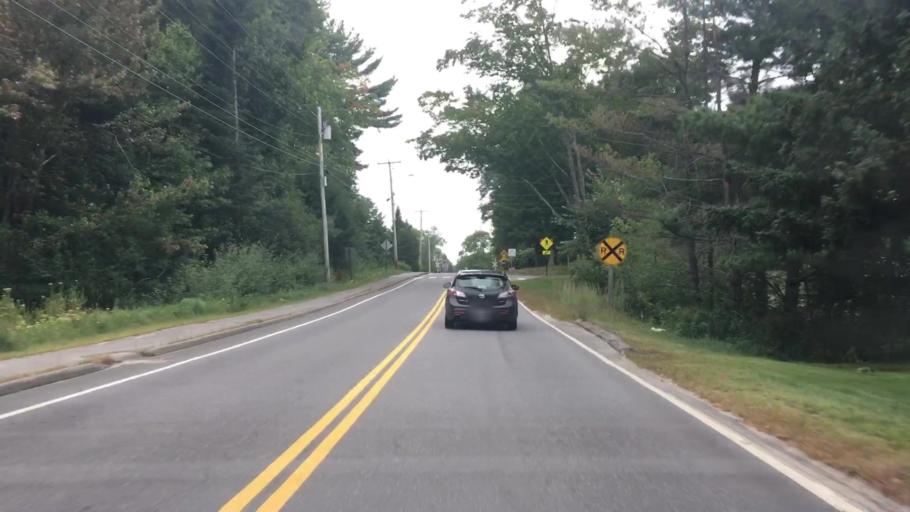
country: US
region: Maine
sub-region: Cumberland County
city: Yarmouth
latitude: 43.8164
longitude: -70.1834
